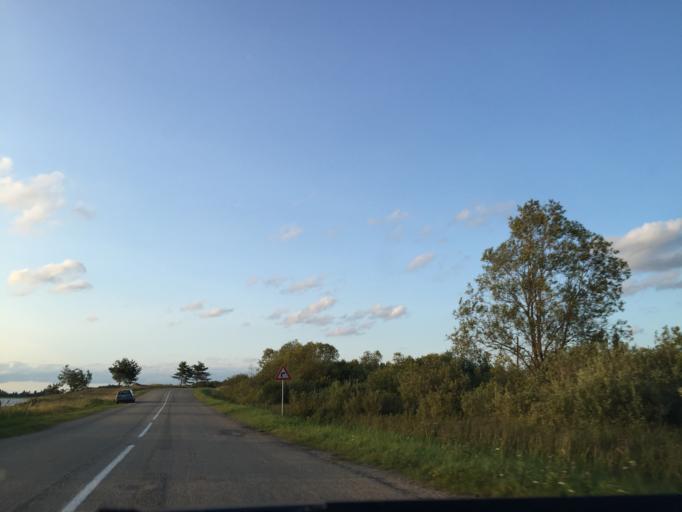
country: LV
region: Dagda
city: Dagda
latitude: 56.3112
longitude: 27.5143
